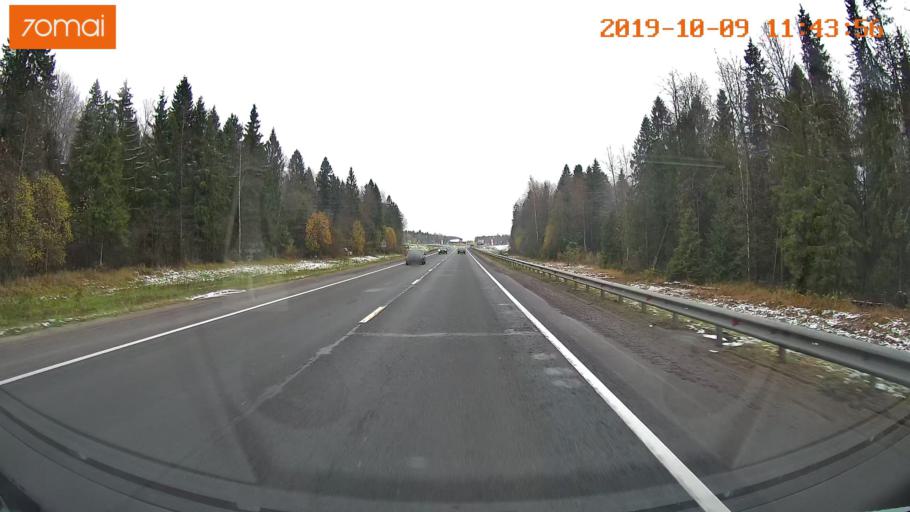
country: RU
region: Vologda
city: Gryazovets
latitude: 58.8899
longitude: 40.1887
